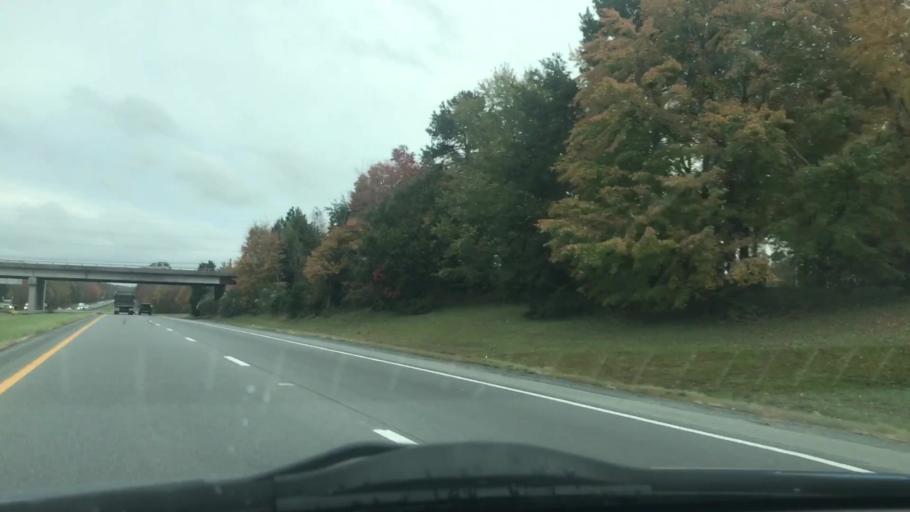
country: US
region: North Carolina
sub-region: Randolph County
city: Asheboro
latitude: 35.7541
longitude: -79.8269
